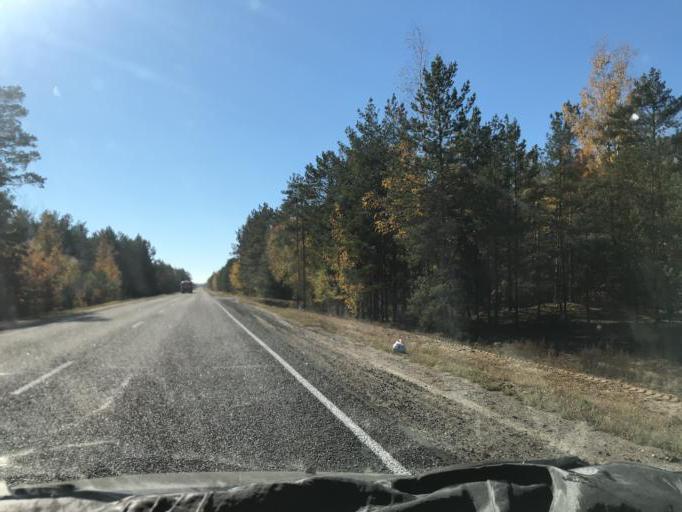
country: BY
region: Gomel
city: Sasnovy Bor
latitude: 52.5286
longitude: 29.3268
